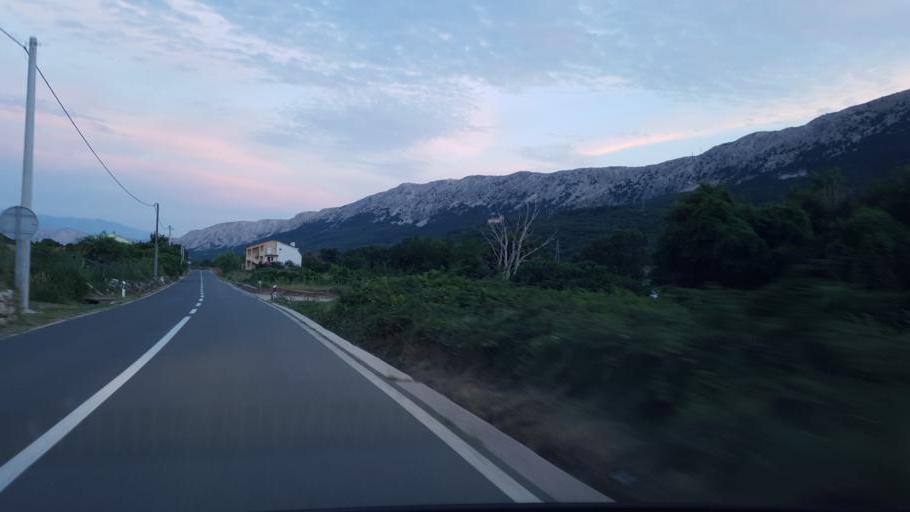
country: HR
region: Primorsko-Goranska
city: Punat
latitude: 44.9882
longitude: 14.7217
